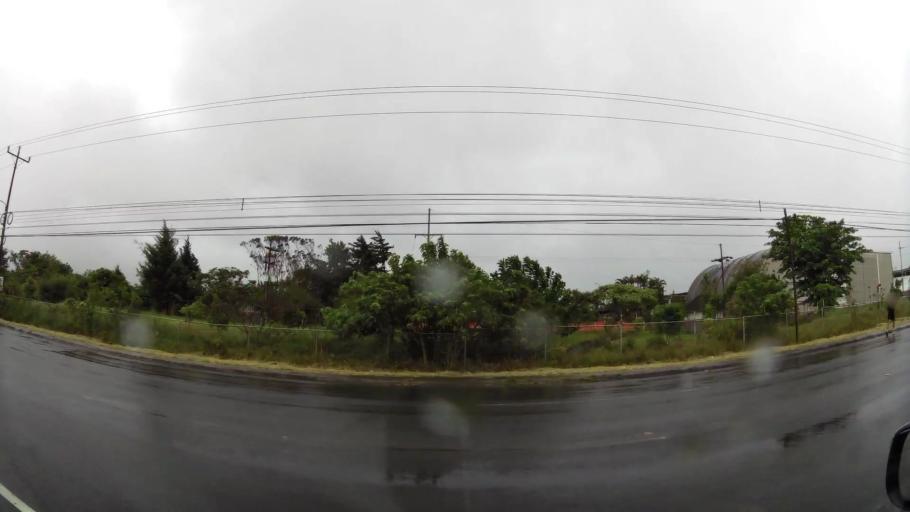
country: CR
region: Cartago
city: Paraiso
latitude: 9.8448
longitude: -83.8886
